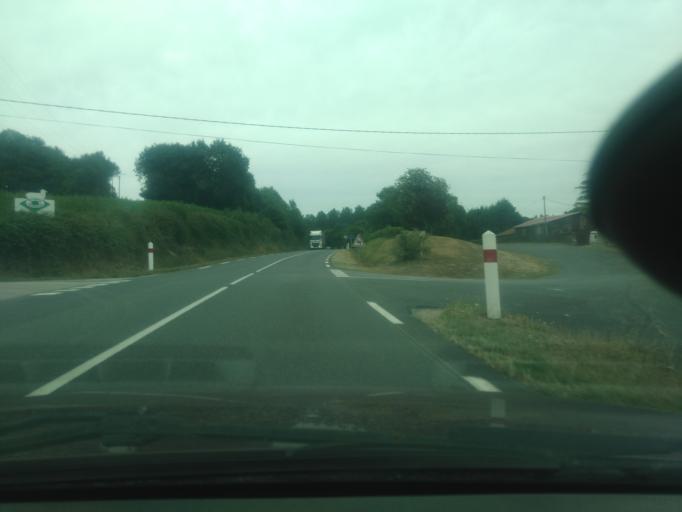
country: FR
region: Pays de la Loire
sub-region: Departement de la Vendee
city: Saint-Pierre-du-Chemin
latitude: 46.6472
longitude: -0.6483
